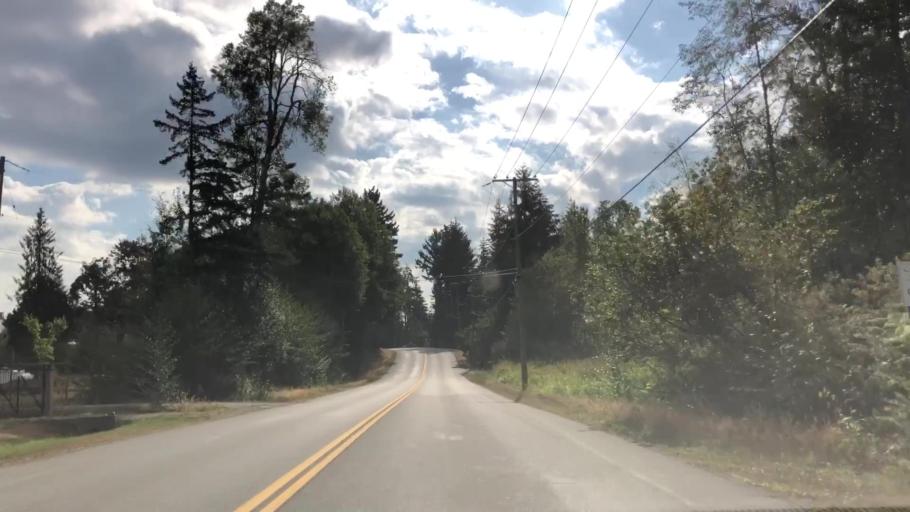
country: CA
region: British Columbia
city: North Saanich
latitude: 48.6871
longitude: -123.5649
